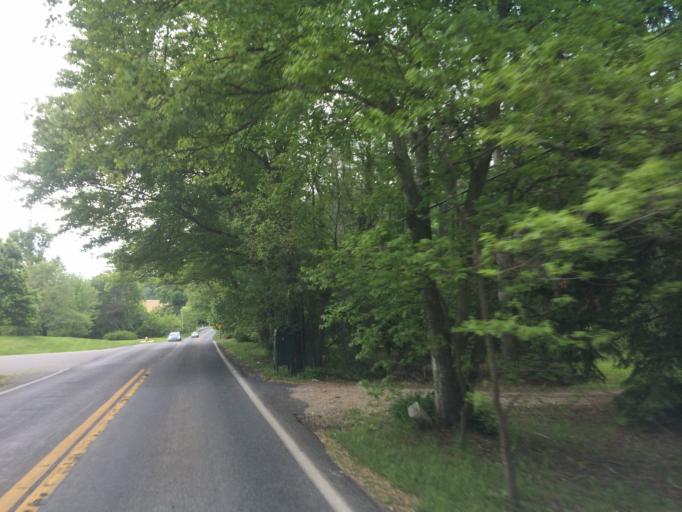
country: US
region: Maryland
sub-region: Howard County
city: Fulton
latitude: 39.1617
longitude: -76.9240
